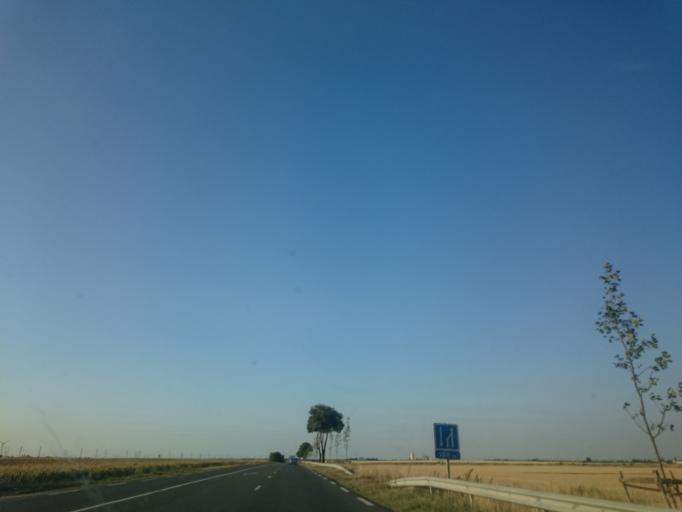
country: FR
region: Centre
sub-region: Departement d'Eure-et-Loir
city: Toury
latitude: 48.2350
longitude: 1.9539
